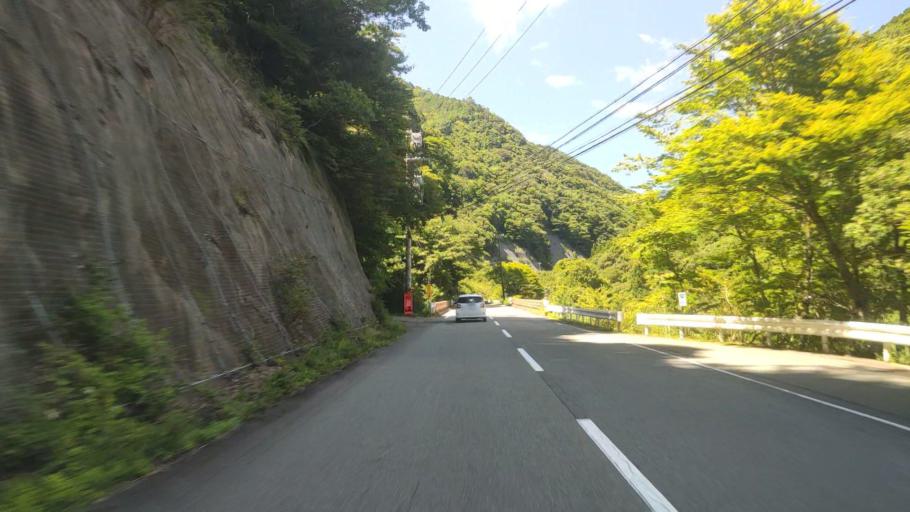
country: JP
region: Nara
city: Yoshino-cho
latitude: 34.2028
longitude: 135.9984
